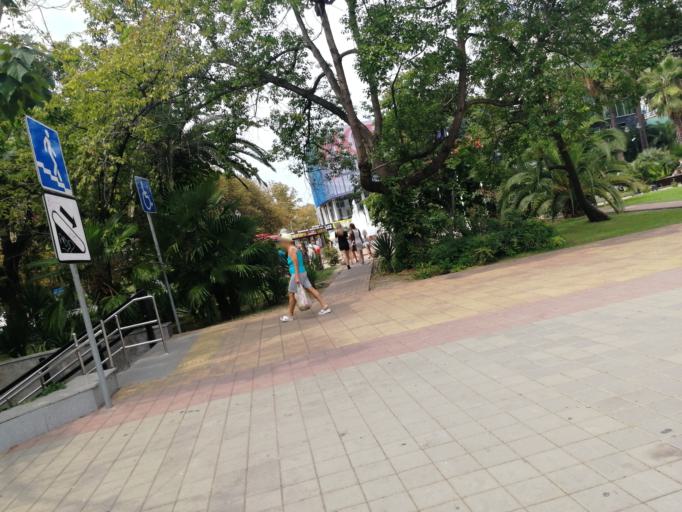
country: RU
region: Krasnodarskiy
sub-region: Sochi City
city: Sochi
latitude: 43.5837
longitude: 39.7211
